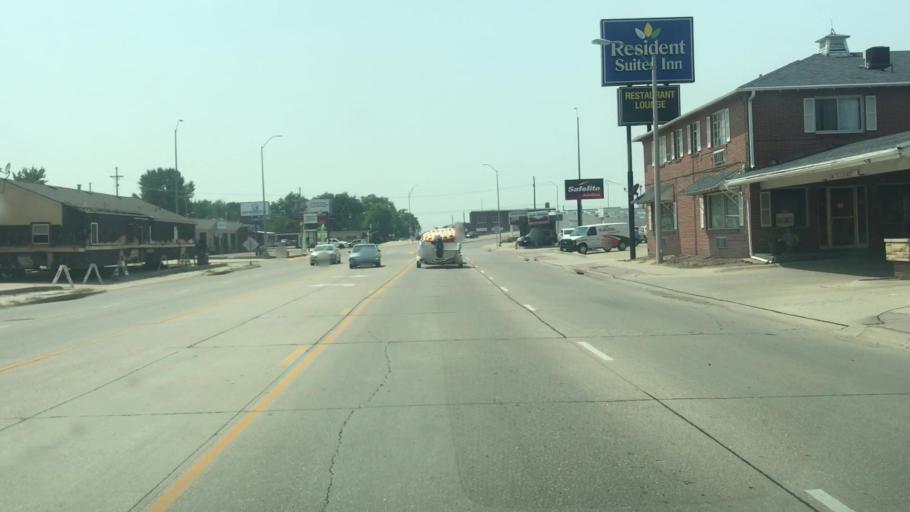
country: US
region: Nebraska
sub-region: Hall County
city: Grand Island
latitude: 40.9159
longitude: -98.3616
